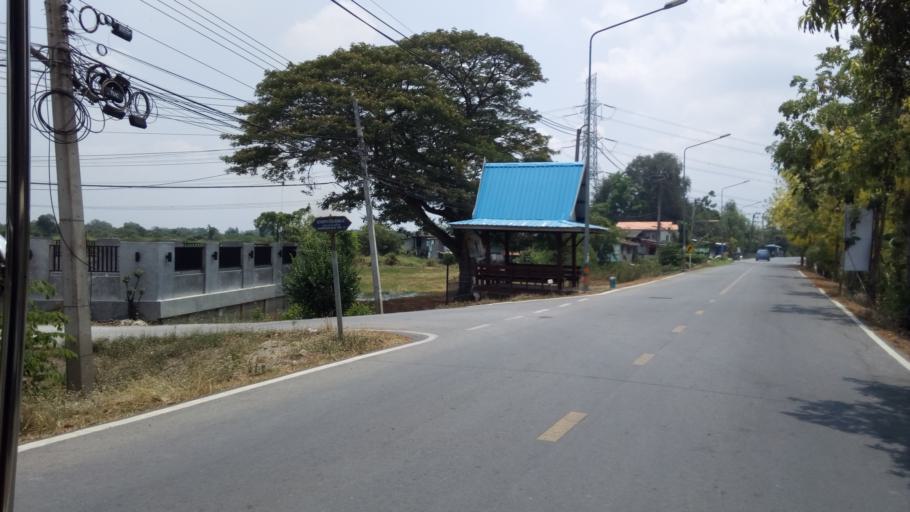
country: TH
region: Pathum Thani
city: Sam Khok
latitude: 14.1067
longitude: 100.5384
